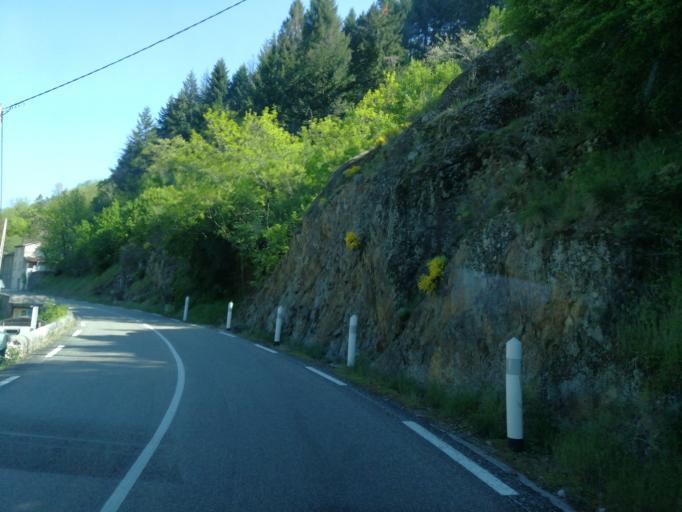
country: FR
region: Rhone-Alpes
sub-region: Departement de l'Ardeche
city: Saint-Sauveur-de-Montagut
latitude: 44.8404
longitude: 4.5757
